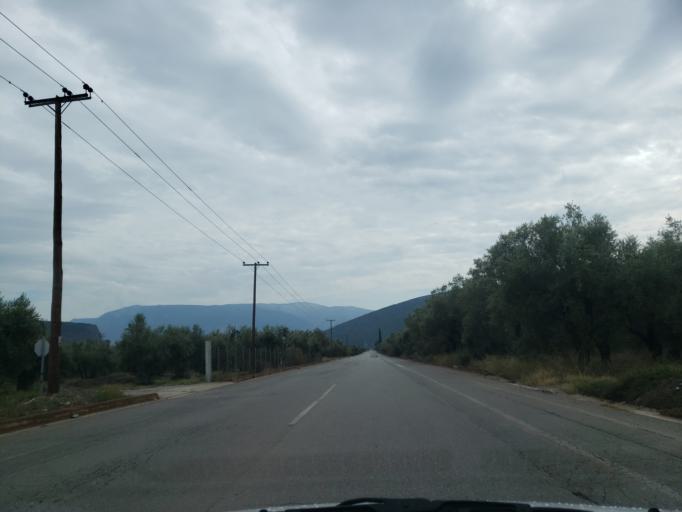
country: GR
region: Central Greece
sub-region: Nomos Fokidos
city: Amfissa
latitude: 38.4978
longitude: 22.4095
